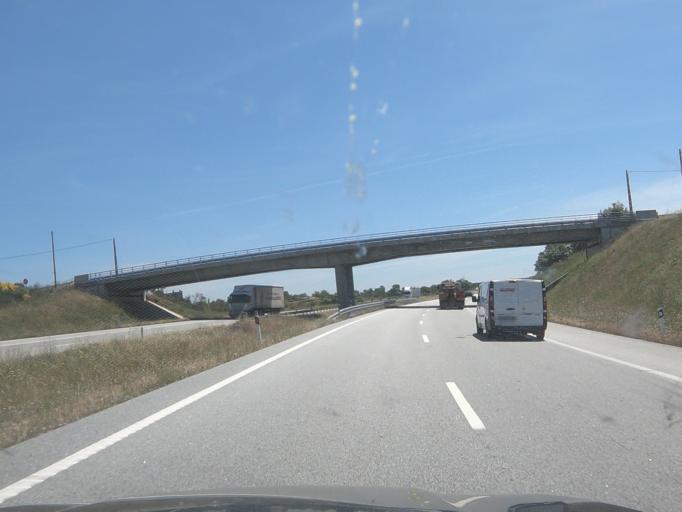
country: PT
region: Guarda
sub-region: Guarda
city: Sequeira
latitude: 40.6026
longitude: -7.1033
